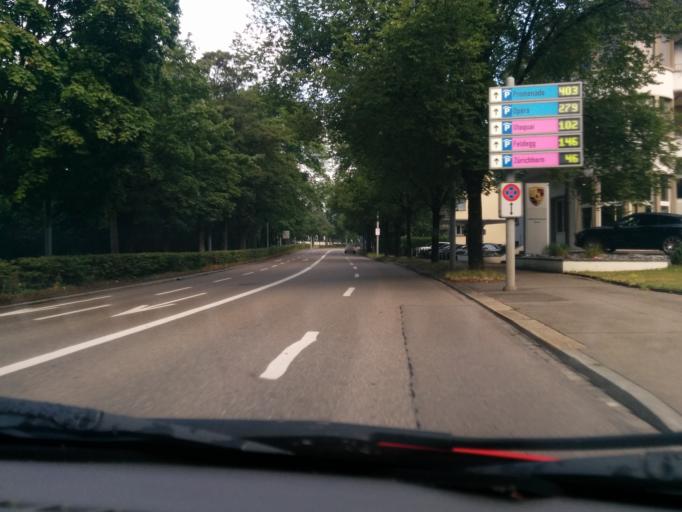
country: CH
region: Zurich
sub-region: Bezirk Zuerich
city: Zuerich (Kreis 8) / Seefeld
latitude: 47.3531
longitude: 8.5566
